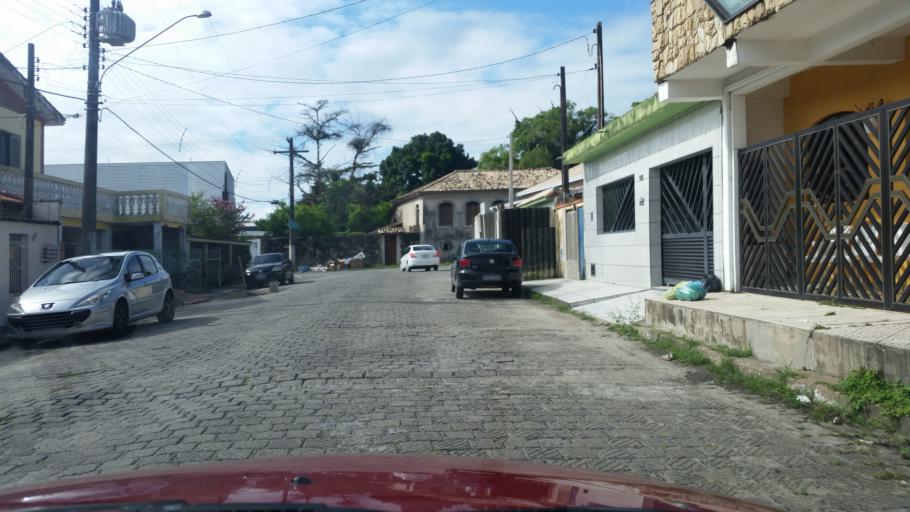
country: BR
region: Sao Paulo
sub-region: Iguape
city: Iguape
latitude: -24.7045
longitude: -47.5551
